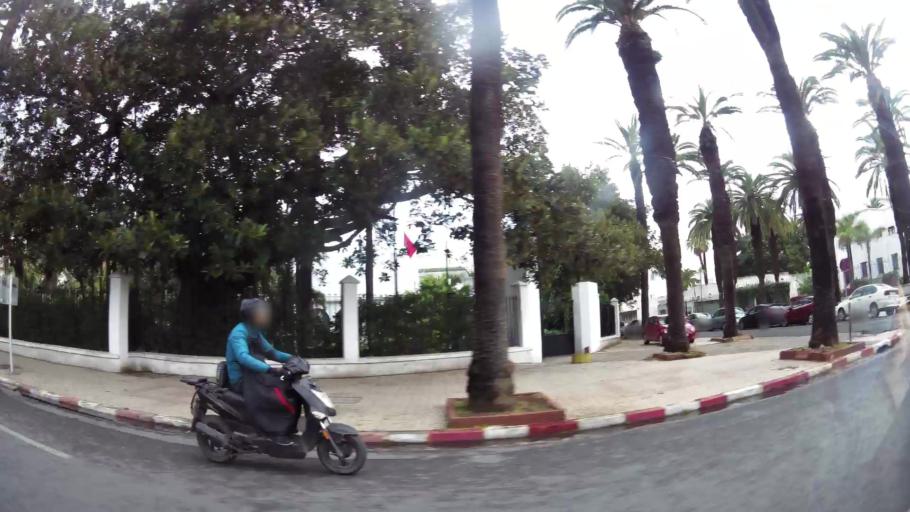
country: MA
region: Grand Casablanca
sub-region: Casablanca
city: Casablanca
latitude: 33.5917
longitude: -7.6234
